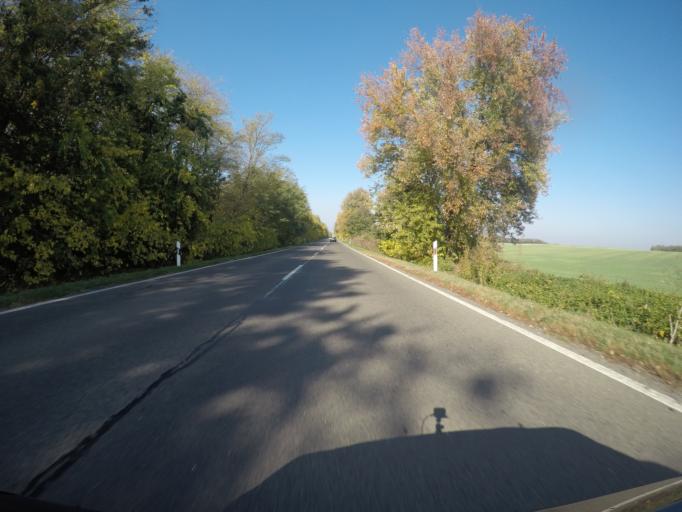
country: HU
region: Tolna
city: Szedres
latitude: 46.5185
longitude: 18.6622
